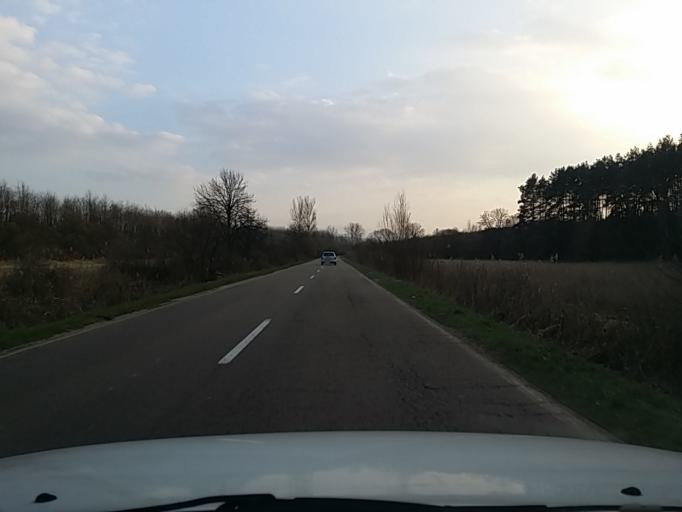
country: HU
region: Heves
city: Petervasara
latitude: 48.0307
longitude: 20.1189
